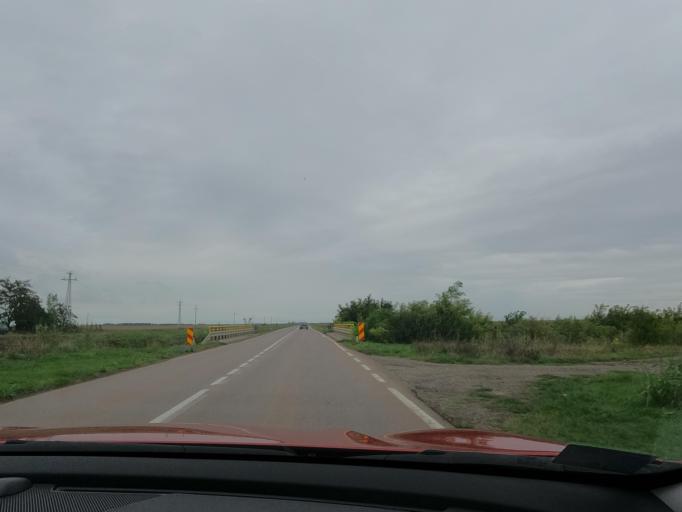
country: RS
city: Banatska Topola
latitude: 45.7197
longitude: 20.4184
